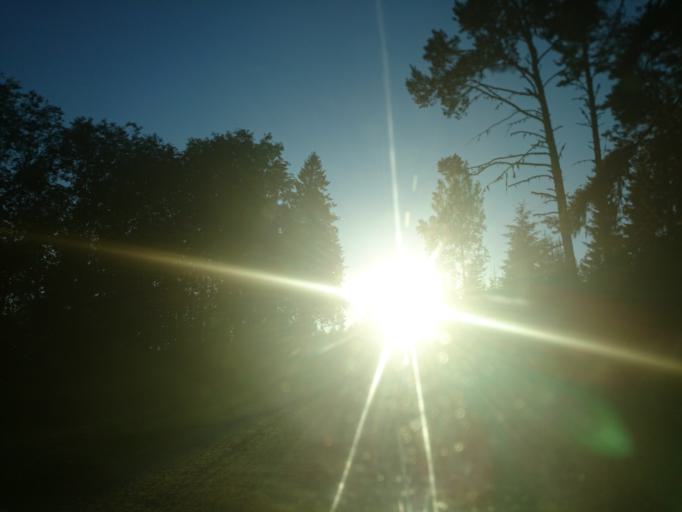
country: SE
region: Vaesternorrland
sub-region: Kramfors Kommun
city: Bollstabruk
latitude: 63.0529
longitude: 17.7132
